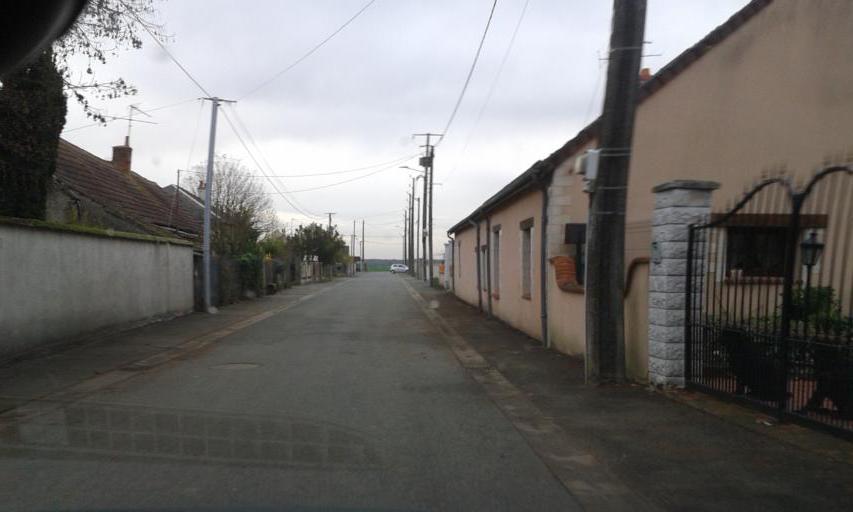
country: FR
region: Centre
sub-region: Departement du Loiret
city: Gidy
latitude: 47.9976
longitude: 1.8299
